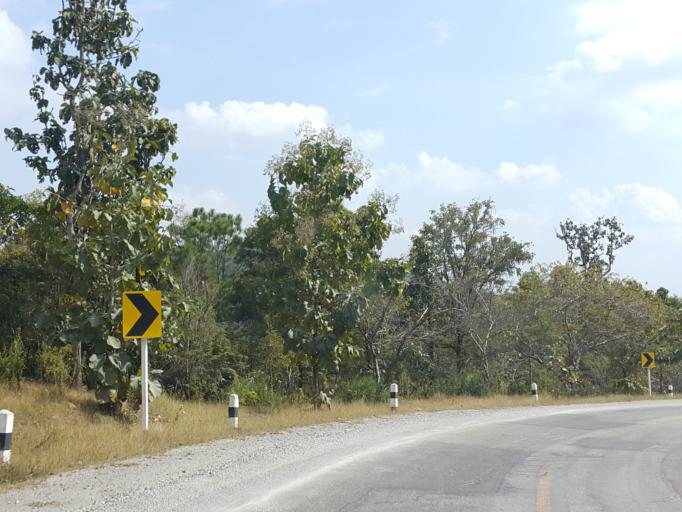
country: TH
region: Chiang Mai
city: Om Koi
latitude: 17.8179
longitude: 98.3676
